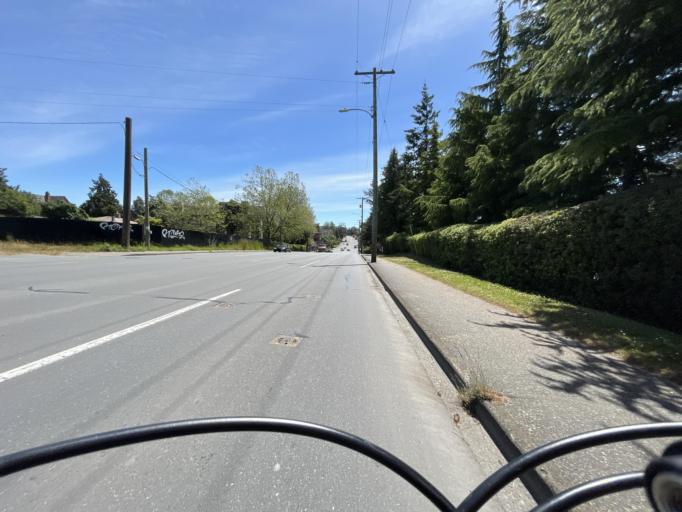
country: CA
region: British Columbia
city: Victoria
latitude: 48.4461
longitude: -123.3941
